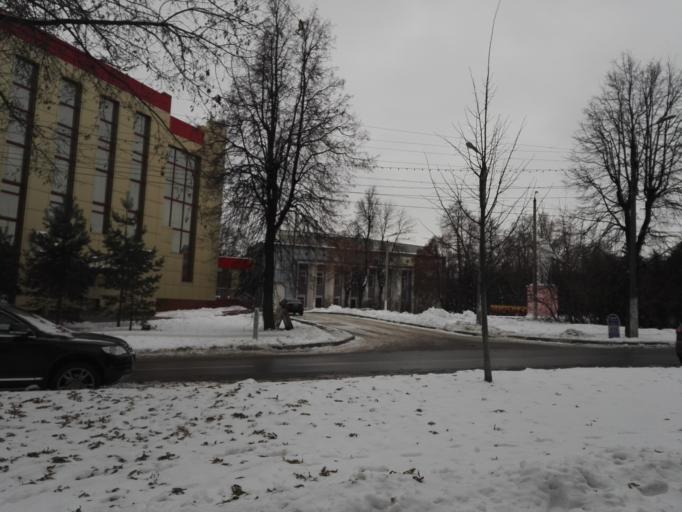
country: RU
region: Tula
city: Novomoskovsk
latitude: 54.0113
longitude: 38.2980
